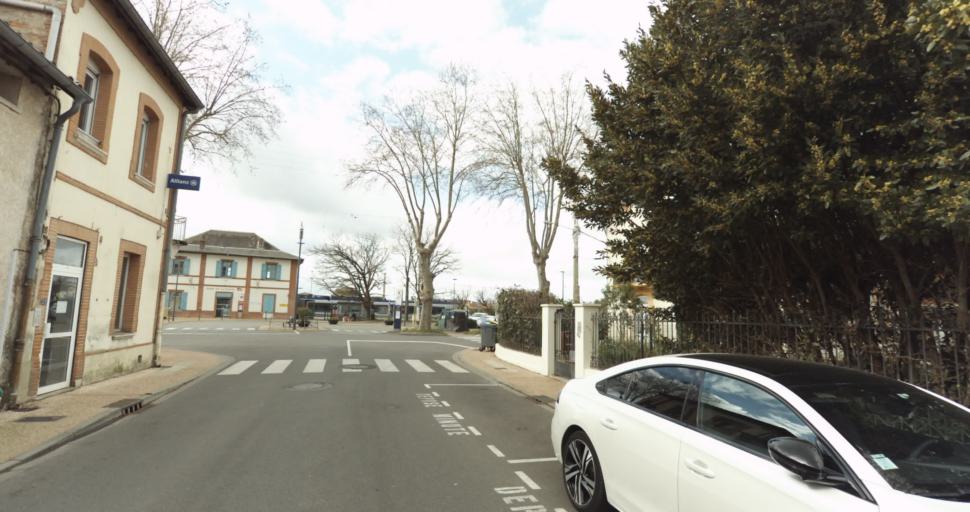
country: FR
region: Midi-Pyrenees
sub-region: Departement de la Haute-Garonne
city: Auterive
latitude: 43.3493
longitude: 1.4695
